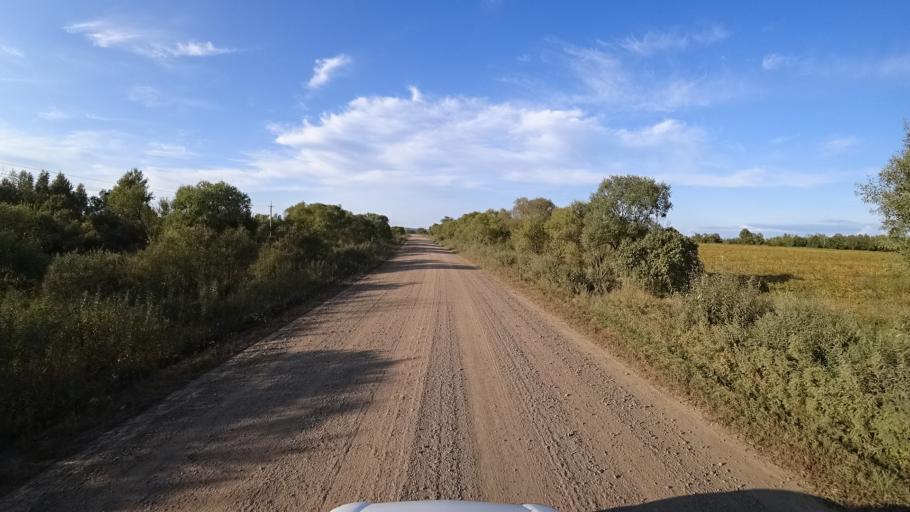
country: RU
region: Amur
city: Arkhara
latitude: 49.3555
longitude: 130.1375
